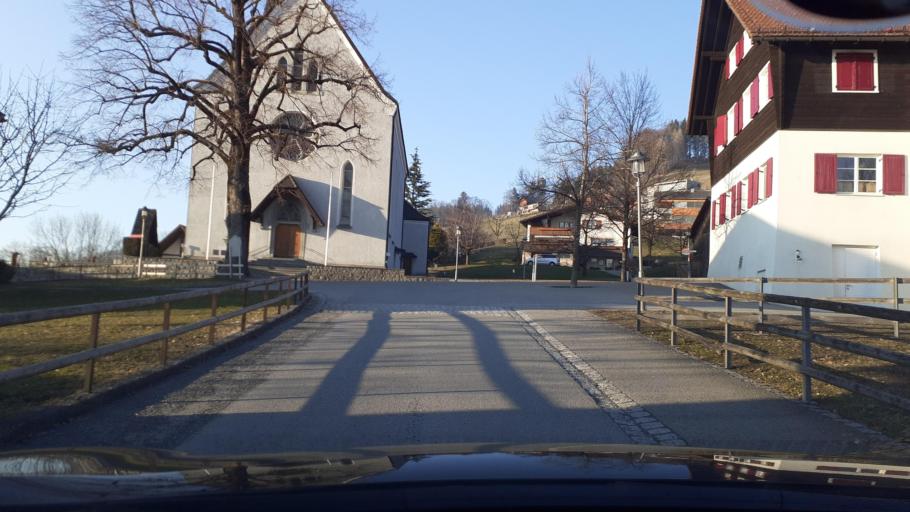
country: AT
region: Vorarlberg
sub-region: Politischer Bezirk Feldkirch
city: Fraxern
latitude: 47.3146
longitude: 9.6734
